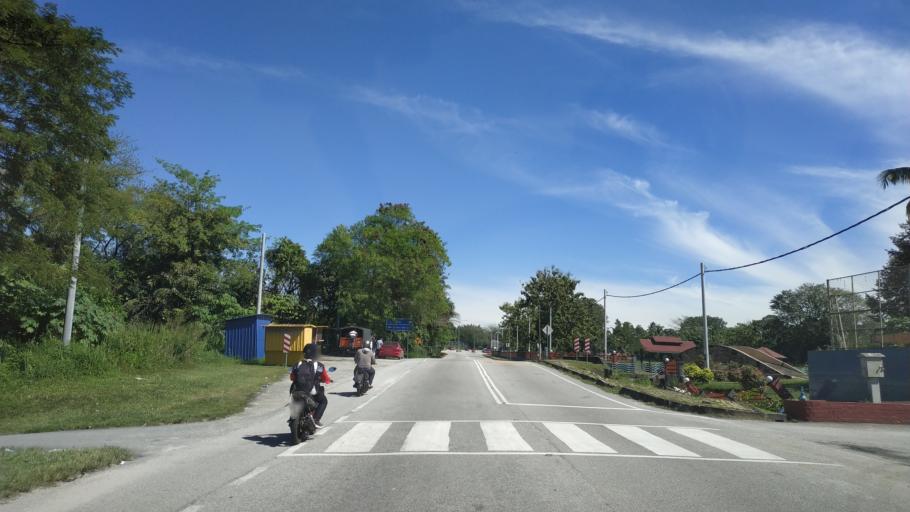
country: MY
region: Kedah
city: Kulim
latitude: 5.3519
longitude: 100.5368
